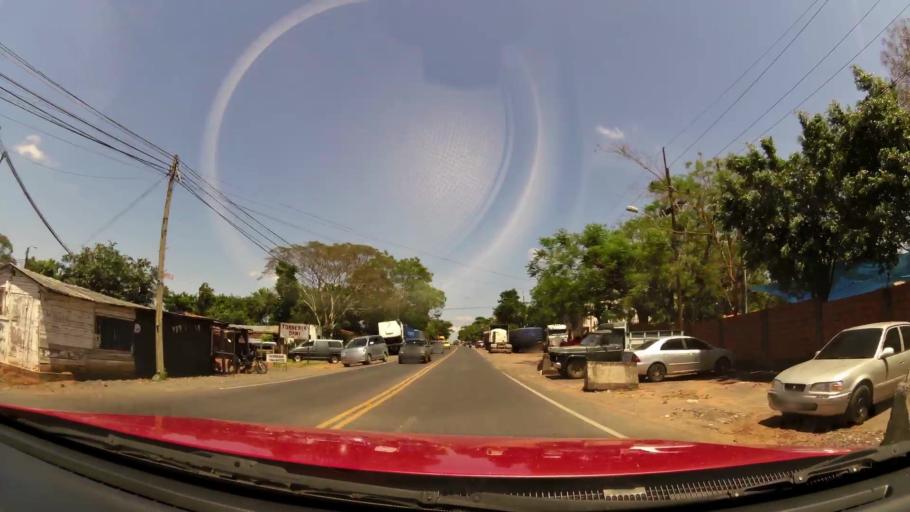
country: PY
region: Central
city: Nemby
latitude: -25.4055
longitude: -57.5434
